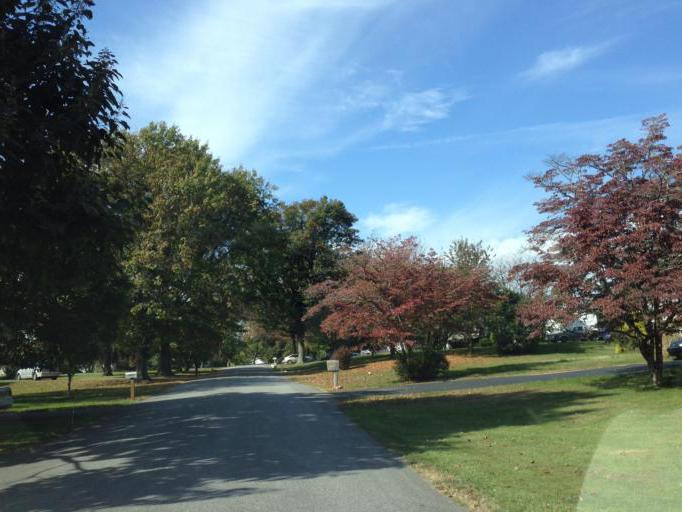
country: US
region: Maryland
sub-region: Howard County
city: Ellicott City
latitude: 39.2497
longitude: -76.8055
